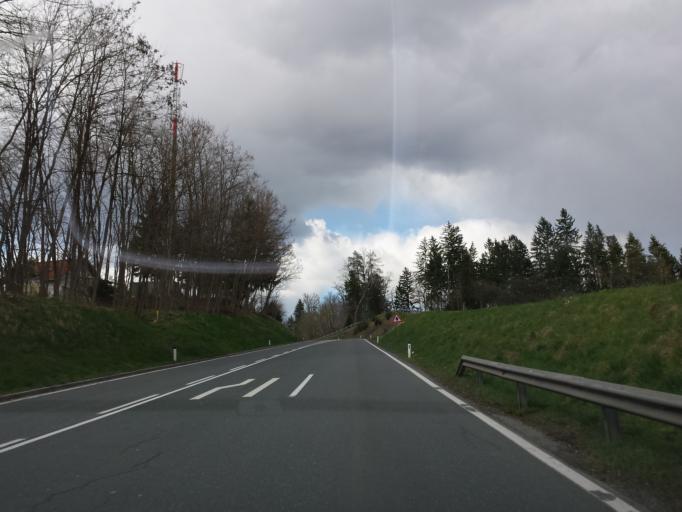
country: AT
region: Styria
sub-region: Politischer Bezirk Deutschlandsberg
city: Rassach
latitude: 46.8495
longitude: 15.2727
